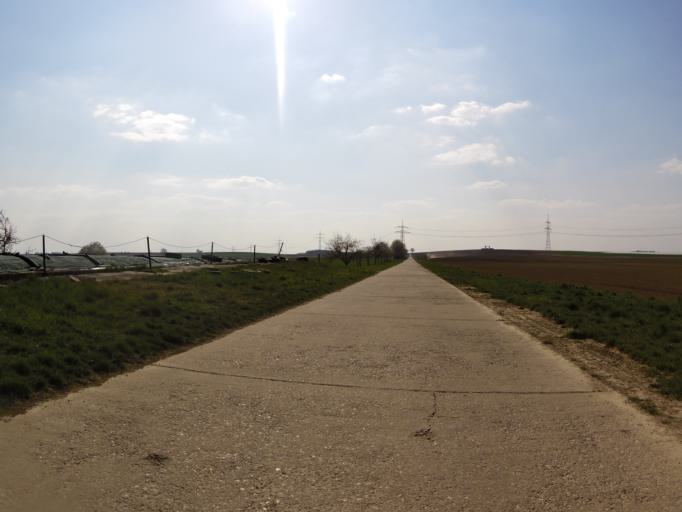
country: DE
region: Bavaria
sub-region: Regierungsbezirk Unterfranken
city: Biebelried
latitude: 49.8190
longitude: 10.0955
